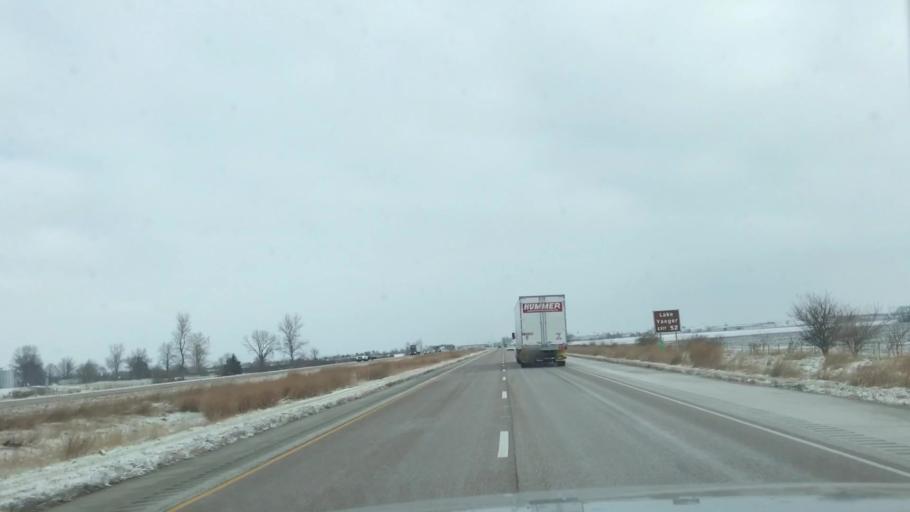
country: US
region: Illinois
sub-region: Montgomery County
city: Litchfield
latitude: 39.1551
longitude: -89.6947
